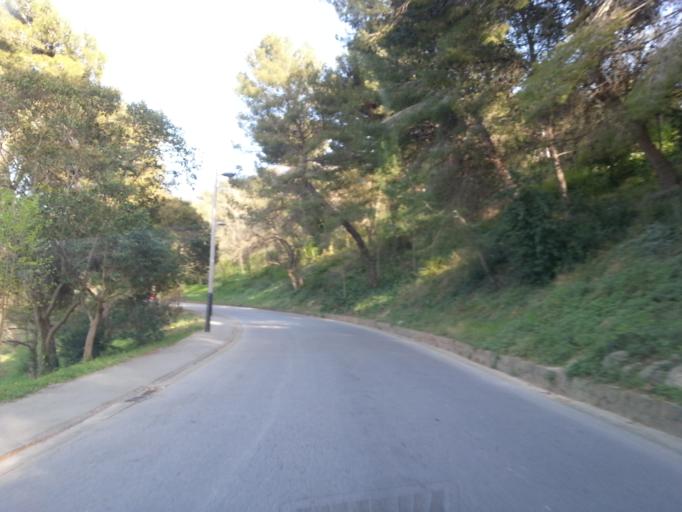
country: ES
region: Catalonia
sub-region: Provincia de Barcelona
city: Sants-Montjuic
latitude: 41.3653
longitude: 2.1639
